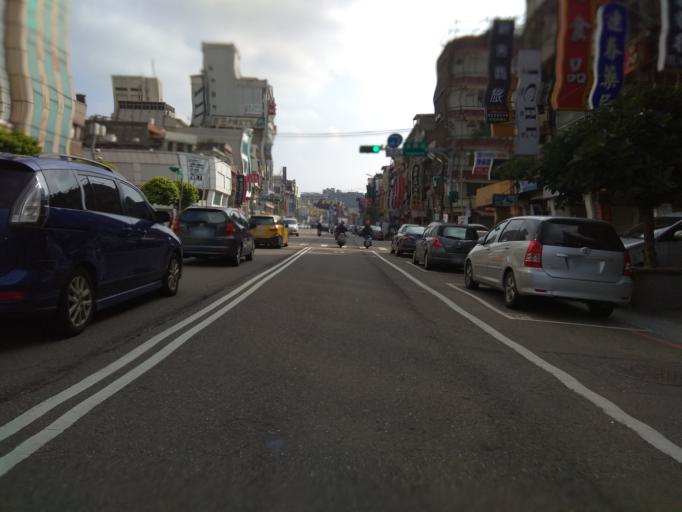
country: TW
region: Taiwan
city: Taoyuan City
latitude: 24.9581
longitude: 121.2199
